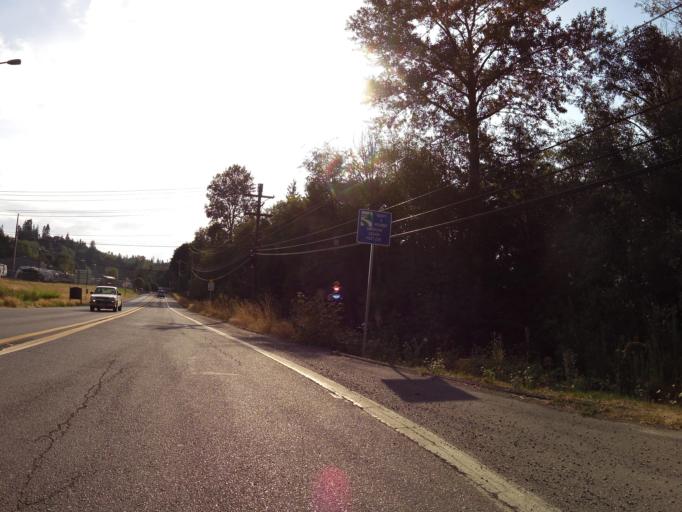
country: US
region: Washington
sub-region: Mason County
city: Belfair
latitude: 47.4327
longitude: -122.8412
